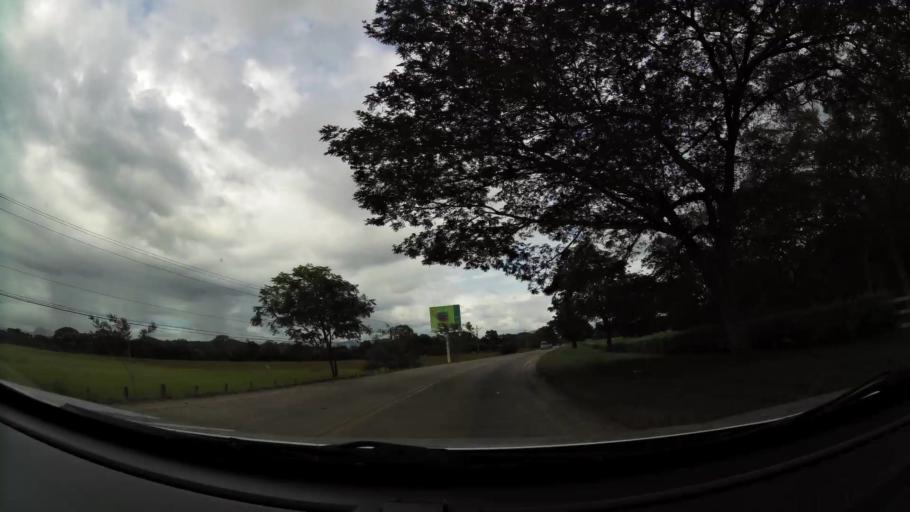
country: CR
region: Guanacaste
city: Juntas
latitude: 10.2590
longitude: -85.0473
